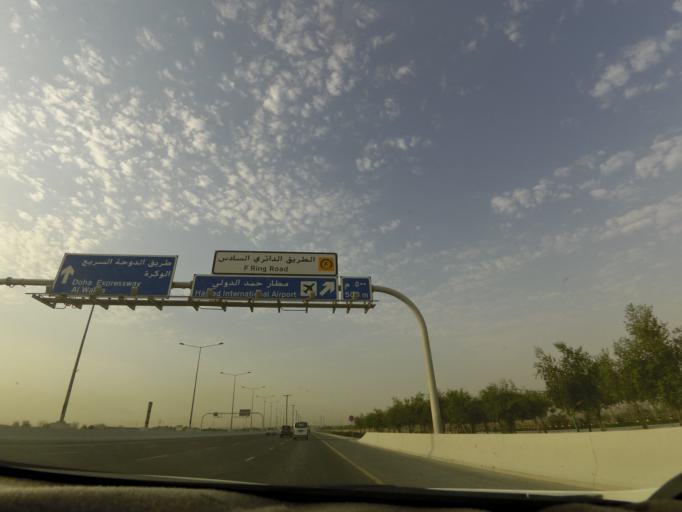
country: QA
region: Baladiyat ad Dawhah
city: Doha
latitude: 25.2502
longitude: 51.5870
